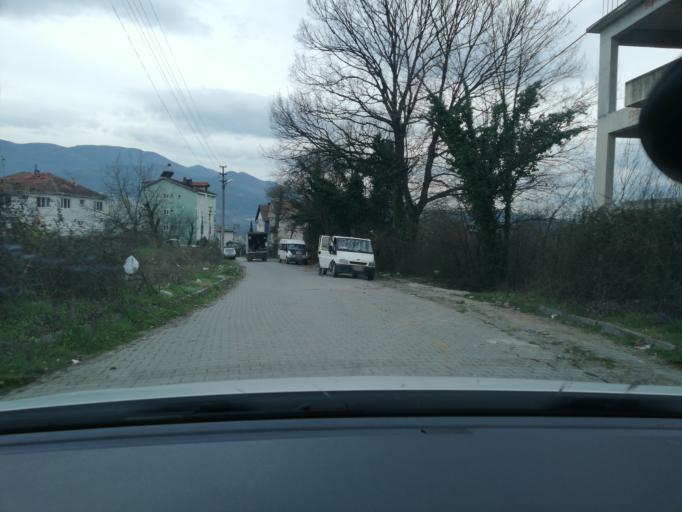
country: TR
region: Zonguldak
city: Gokcebey
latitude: 41.3095
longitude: 32.1421
